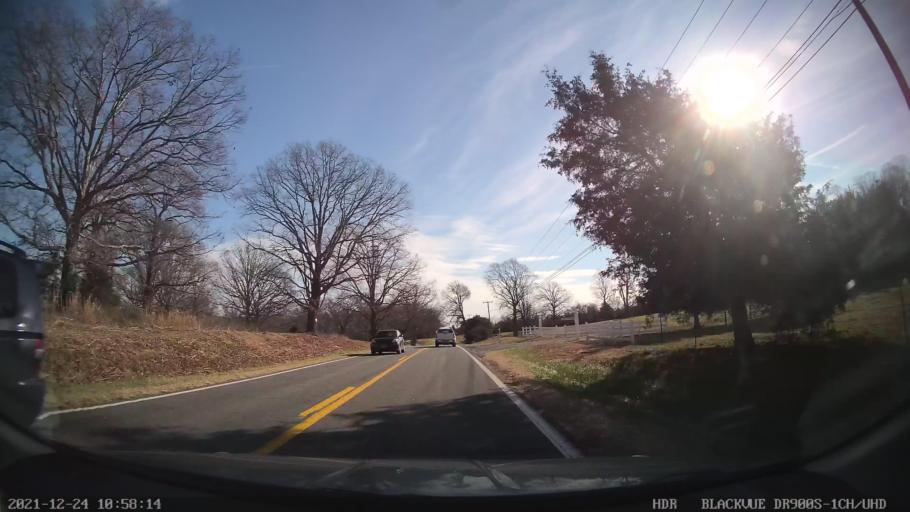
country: US
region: Virginia
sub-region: Goochland County
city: Goochland
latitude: 37.6902
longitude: -77.7508
